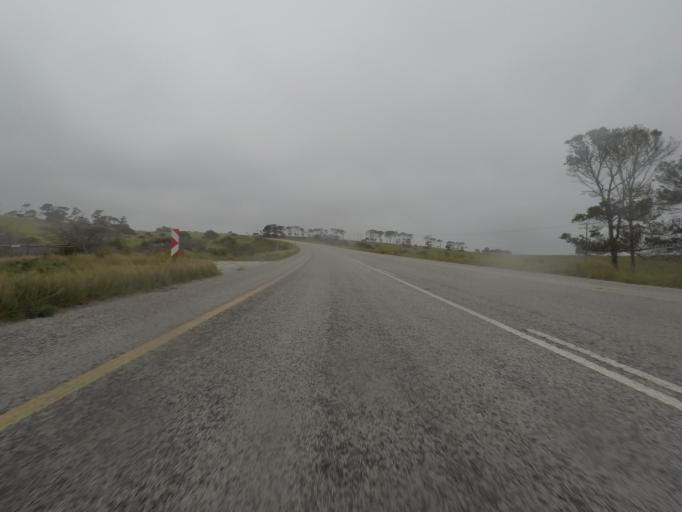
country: ZA
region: Eastern Cape
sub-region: Cacadu District Municipality
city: Grahamstown
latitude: -33.6439
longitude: 26.3439
